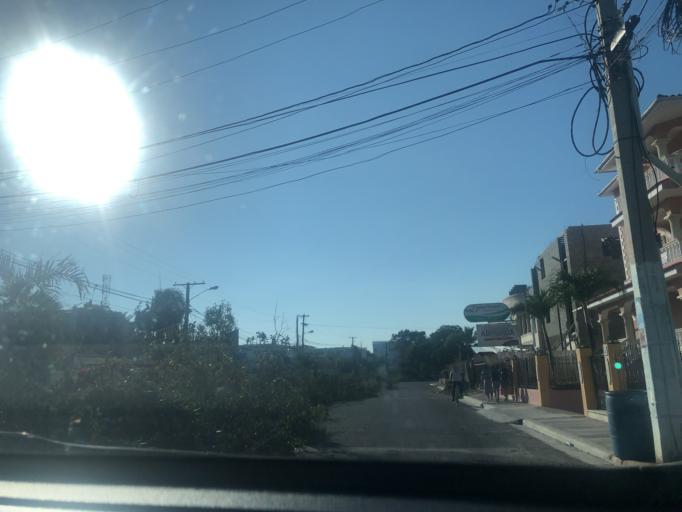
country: DO
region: Santo Domingo
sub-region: Santo Domingo
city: Boca Chica
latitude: 18.4505
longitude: -69.6071
